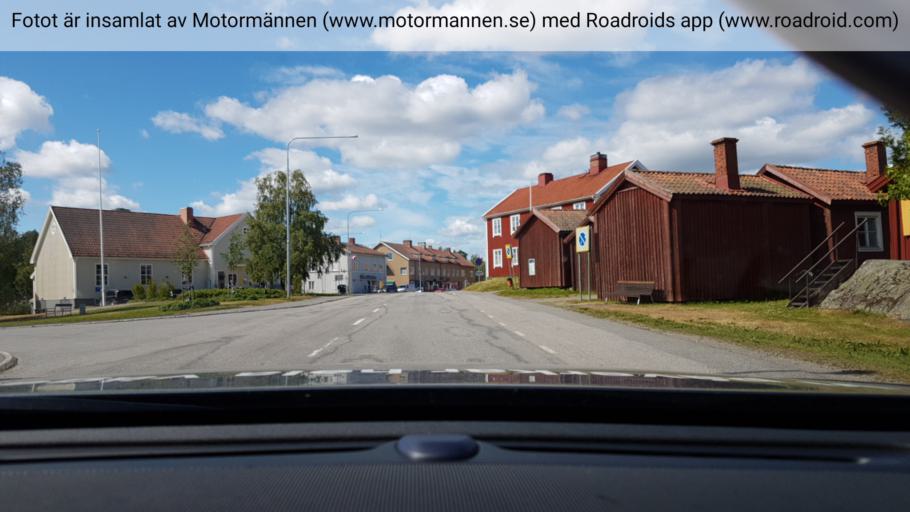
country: SE
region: Vaesterbotten
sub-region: Skelleftea Kommun
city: Burea
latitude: 64.3688
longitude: 21.3175
